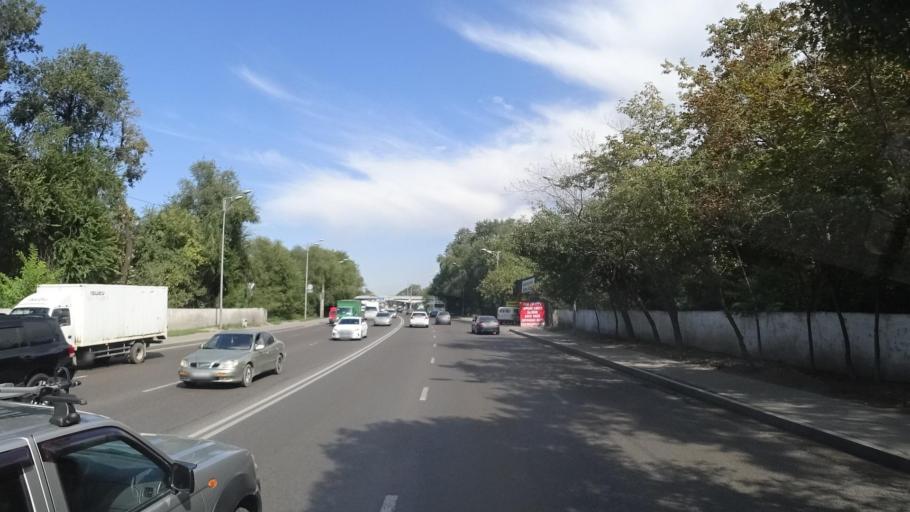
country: KZ
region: Almaty Qalasy
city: Almaty
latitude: 43.2782
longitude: 76.9023
